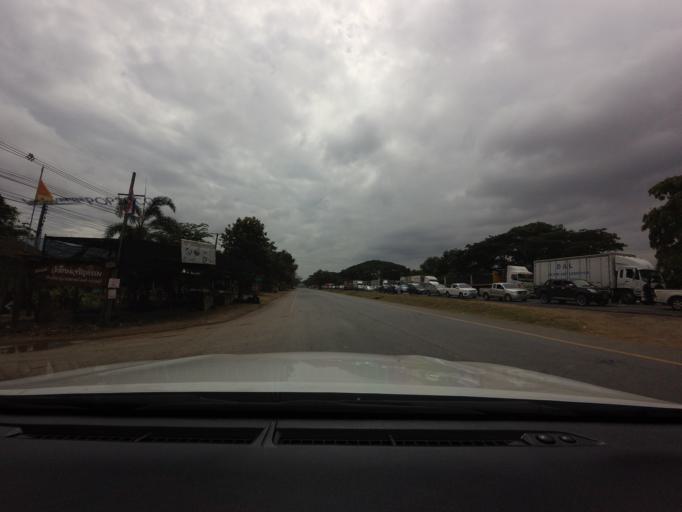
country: TH
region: Nakhon Ratchasima
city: Wang Nam Khiao
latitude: 14.2768
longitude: 101.8941
